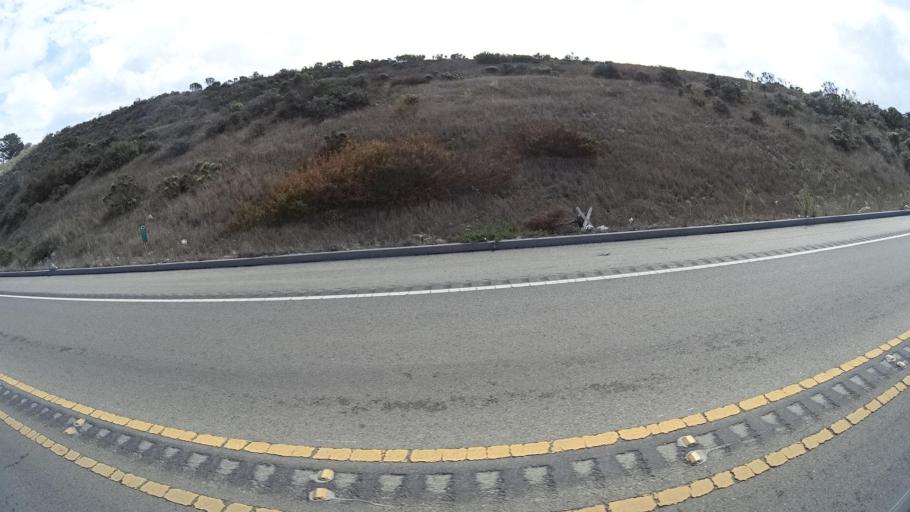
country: US
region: California
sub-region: Monterey County
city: Marina
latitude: 36.6735
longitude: -121.7549
